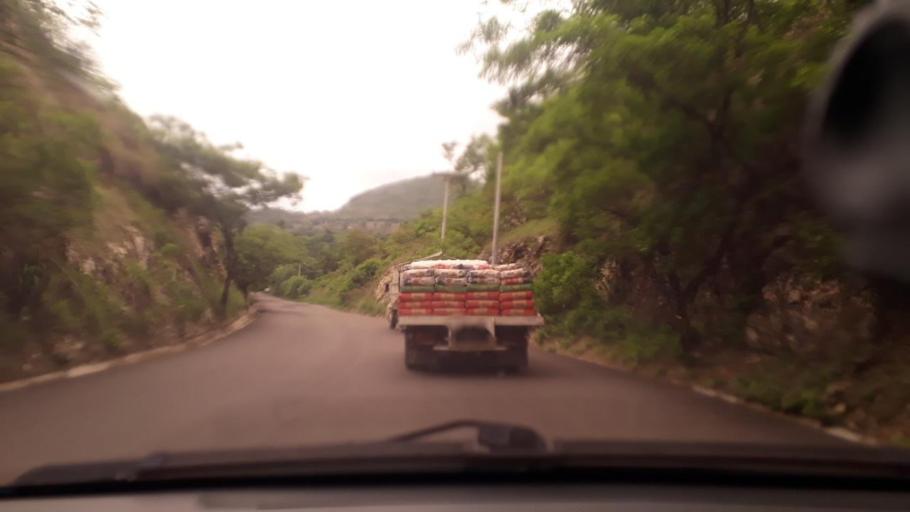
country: GT
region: Chiquimula
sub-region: Municipio de San Juan Ermita
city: San Juan Ermita
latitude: 14.7346
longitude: -89.4706
